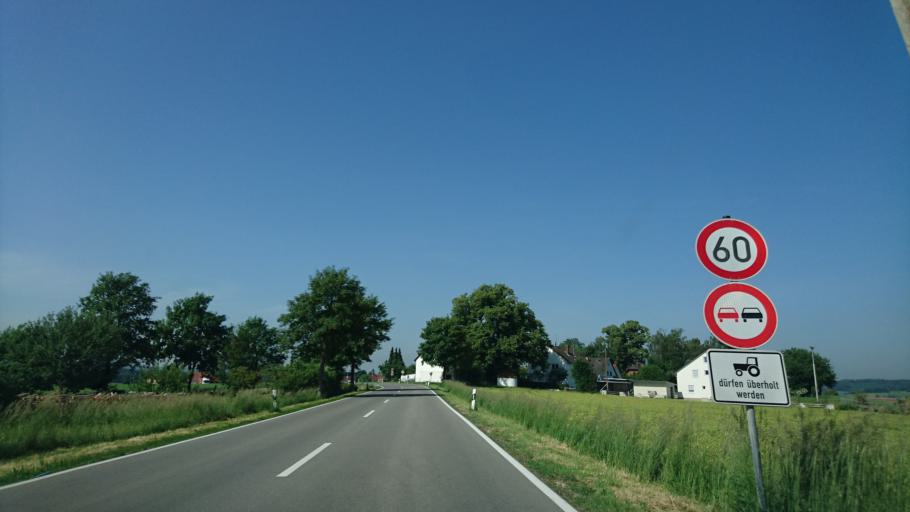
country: DE
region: Bavaria
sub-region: Swabia
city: Ustersbach
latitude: 48.3576
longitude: 10.6442
